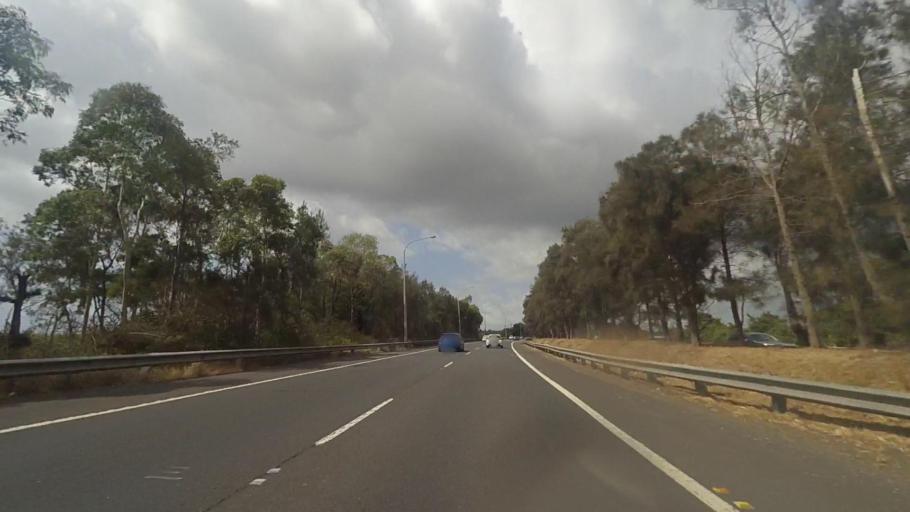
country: AU
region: New South Wales
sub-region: Wollongong
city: Mount Saint Thomas
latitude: -34.4522
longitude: 150.8593
